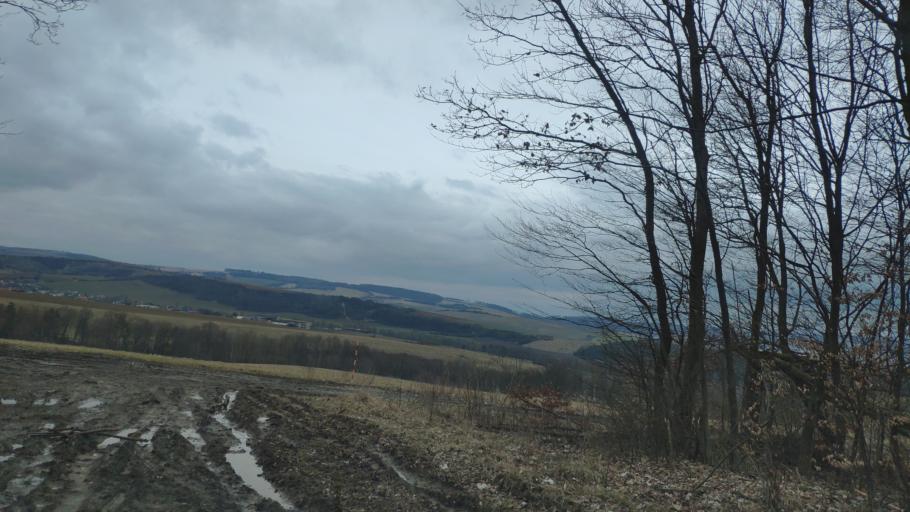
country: SK
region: Presovsky
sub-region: Okres Presov
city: Presov
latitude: 49.0745
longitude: 21.2756
